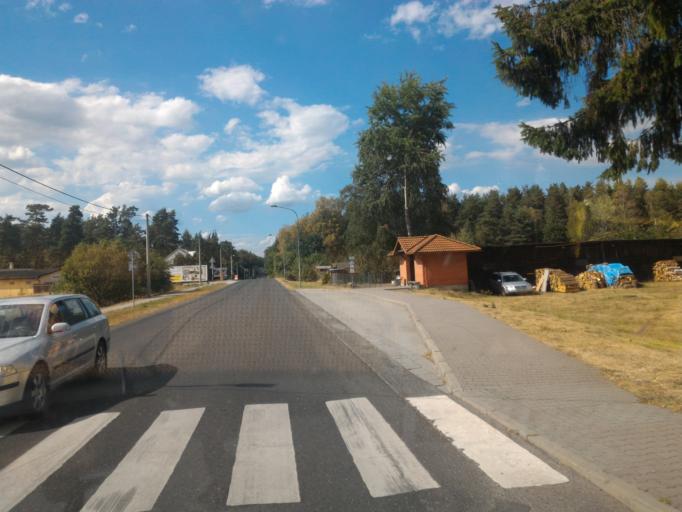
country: CZ
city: Mimon
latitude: 50.6311
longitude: 14.7524
